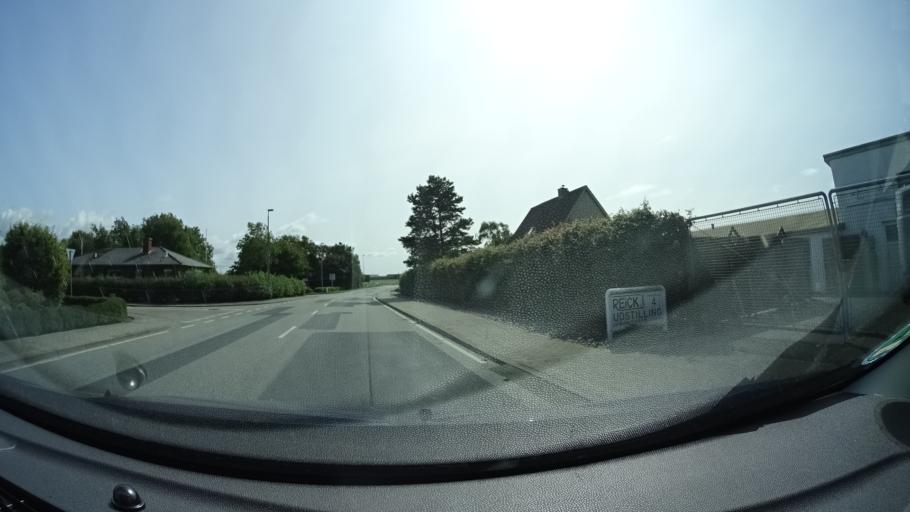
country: DE
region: Schleswig-Holstein
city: Rodenas
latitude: 54.9620
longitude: 8.7036
